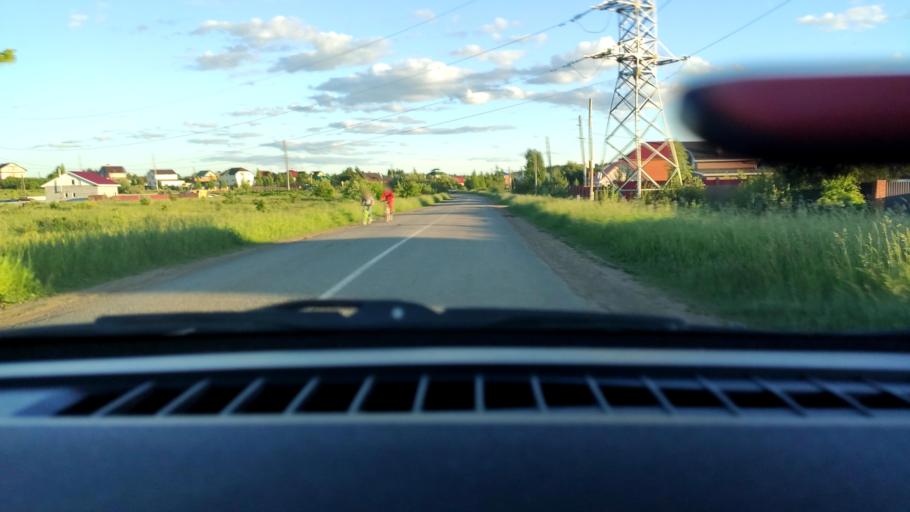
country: RU
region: Perm
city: Kultayevo
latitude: 57.9318
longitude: 55.8631
